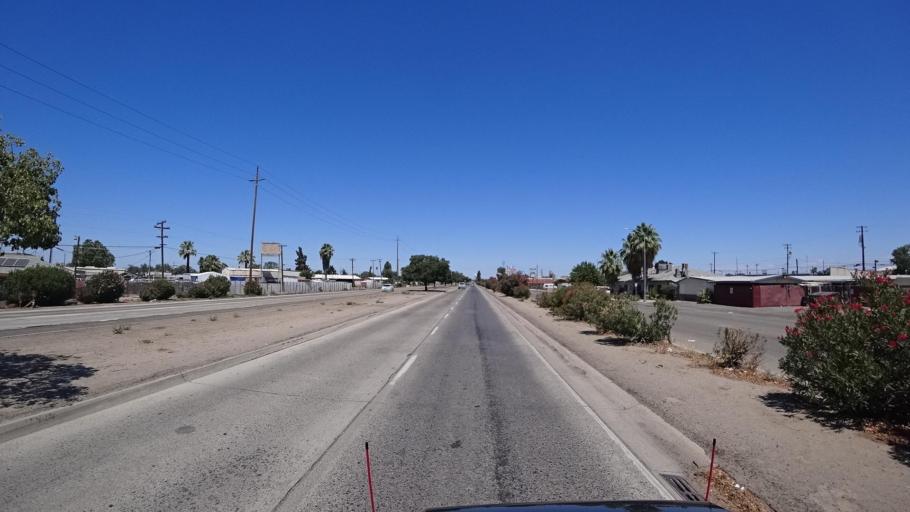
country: US
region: California
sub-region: Fresno County
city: Fresno
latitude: 36.7151
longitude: -119.7770
